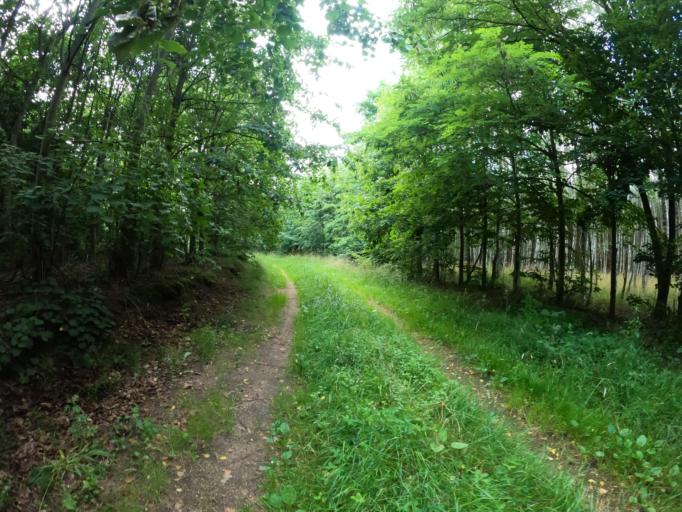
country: PL
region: West Pomeranian Voivodeship
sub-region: Powiat szczecinecki
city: Grzmiaca
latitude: 53.8287
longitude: 16.4643
